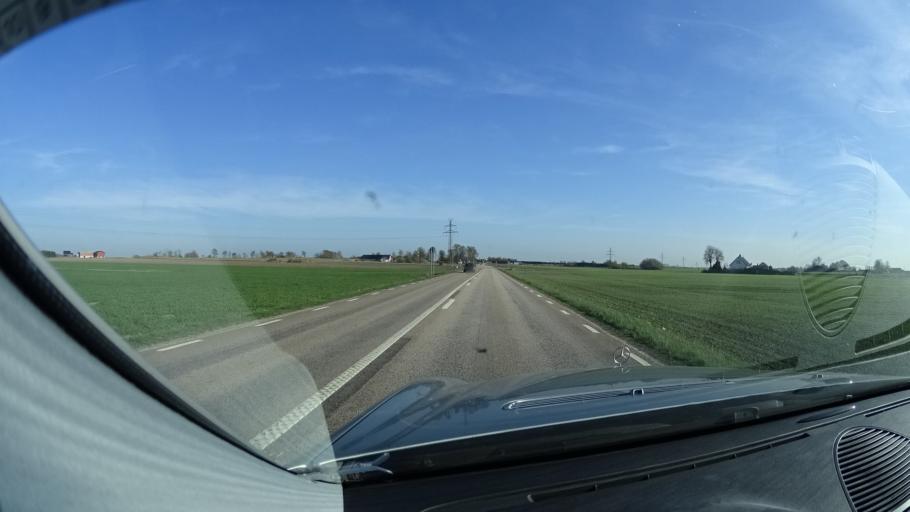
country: SE
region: Skane
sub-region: Landskrona
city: Asmundtorp
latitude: 55.9735
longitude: 12.9391
